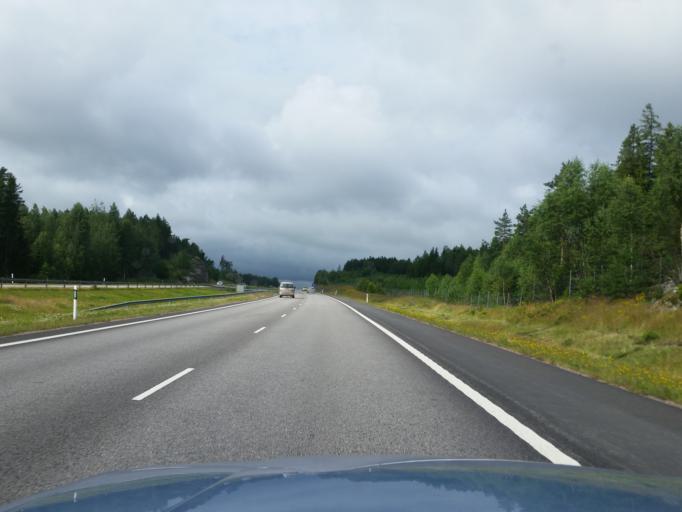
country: FI
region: Varsinais-Suomi
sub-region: Turku
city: Paimio
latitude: 60.4285
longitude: 22.8383
